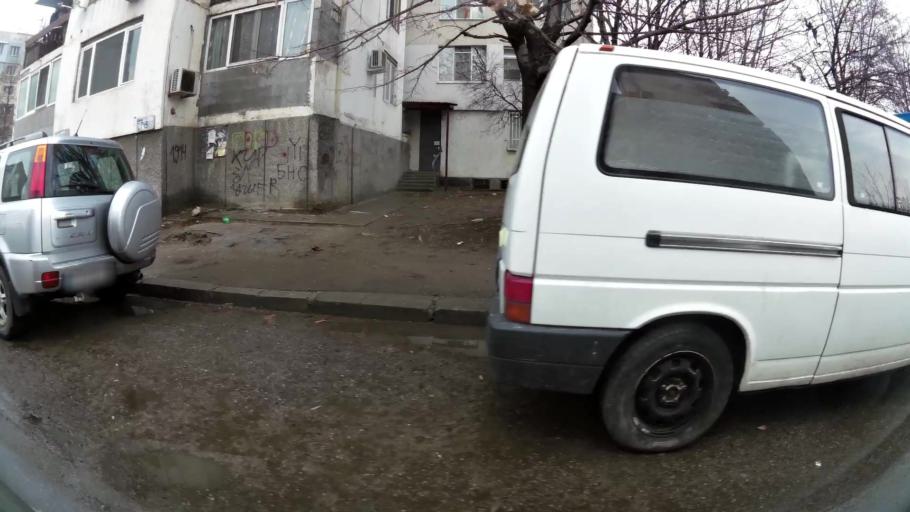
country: BG
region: Sofia-Capital
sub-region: Stolichna Obshtina
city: Sofia
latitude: 42.7127
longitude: 23.2654
